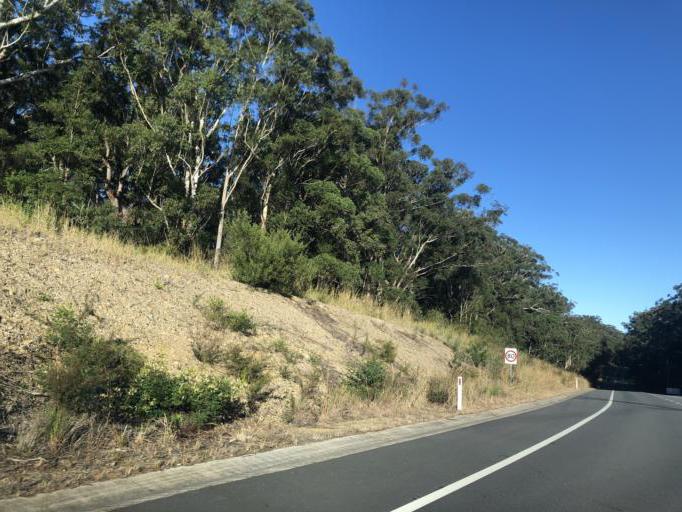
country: AU
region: New South Wales
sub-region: Nambucca Shire
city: Nambucca
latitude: -30.5451
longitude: 153.0067
